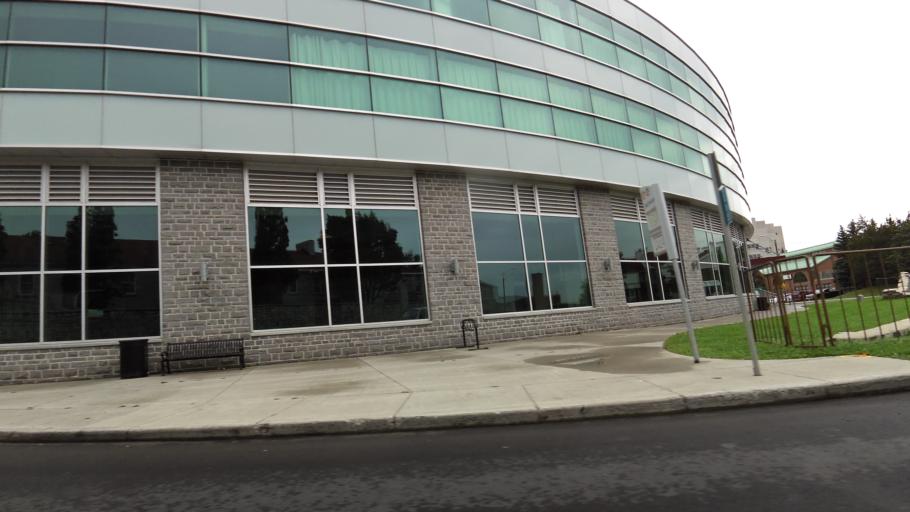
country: CA
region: Ontario
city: Kingston
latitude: 44.2334
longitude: -76.4789
